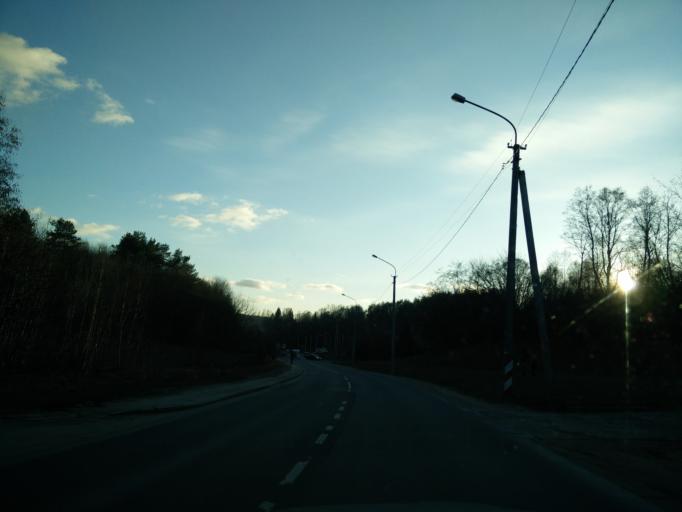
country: LT
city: Skaidiskes
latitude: 54.7001
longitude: 25.4031
